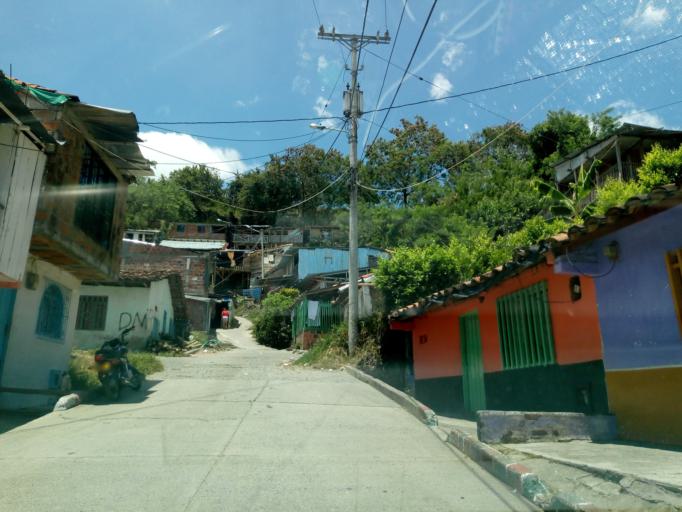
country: CO
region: Valle del Cauca
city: Cartago
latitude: 4.7238
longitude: -75.9044
